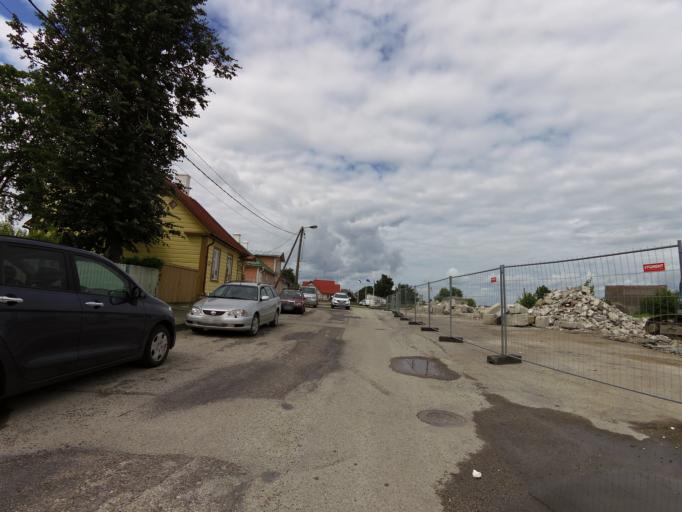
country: EE
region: Laeaene
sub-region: Haapsalu linn
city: Haapsalu
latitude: 58.9549
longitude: 23.5296
